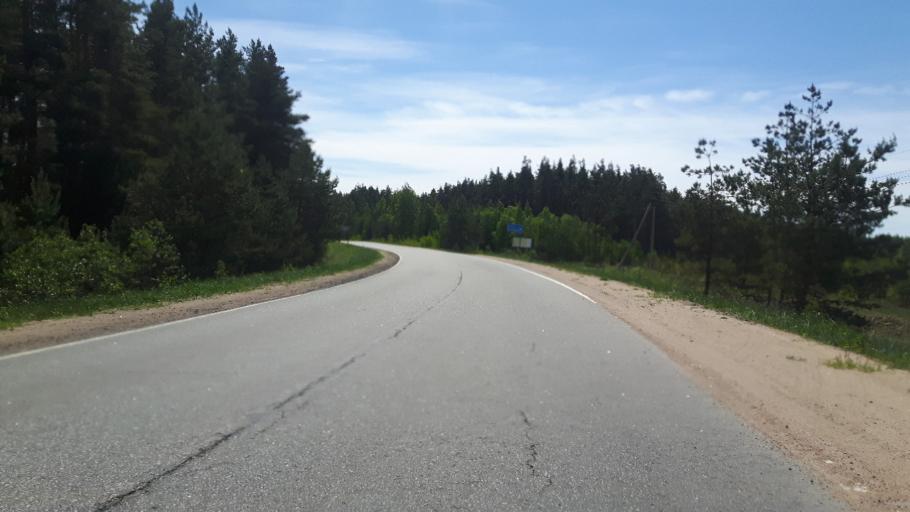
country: EE
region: Ida-Virumaa
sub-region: Narva-Joesuu linn
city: Narva-Joesuu
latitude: 59.5691
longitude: 28.1527
